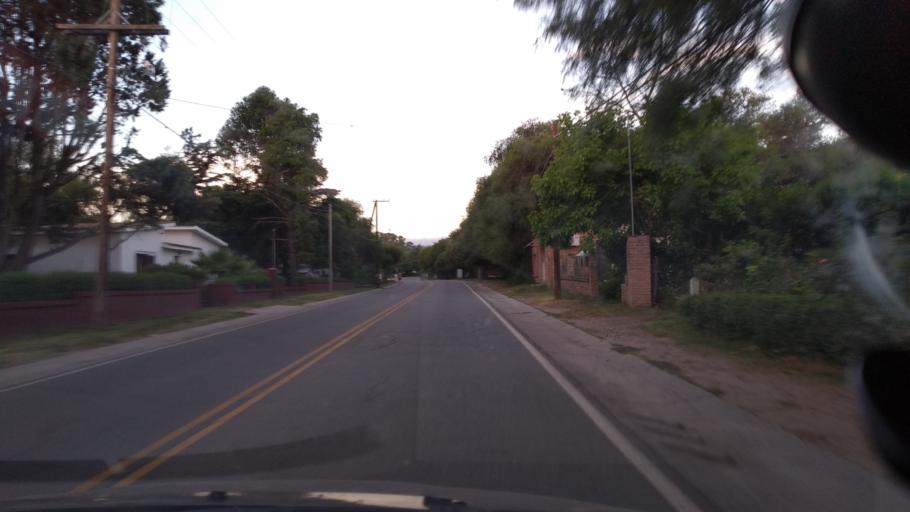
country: AR
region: Cordoba
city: Villa Las Rosas
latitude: -31.9536
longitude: -65.0606
